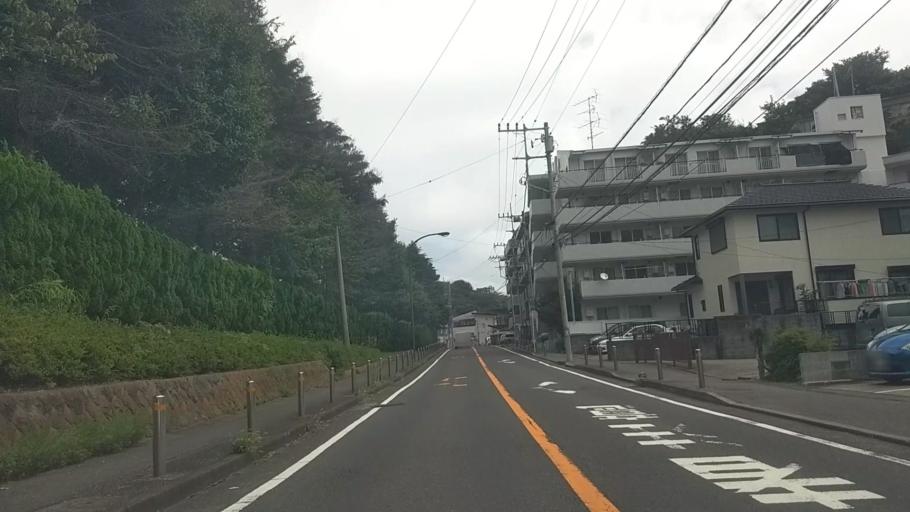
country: JP
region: Kanagawa
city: Yokosuka
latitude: 35.2714
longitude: 139.6607
